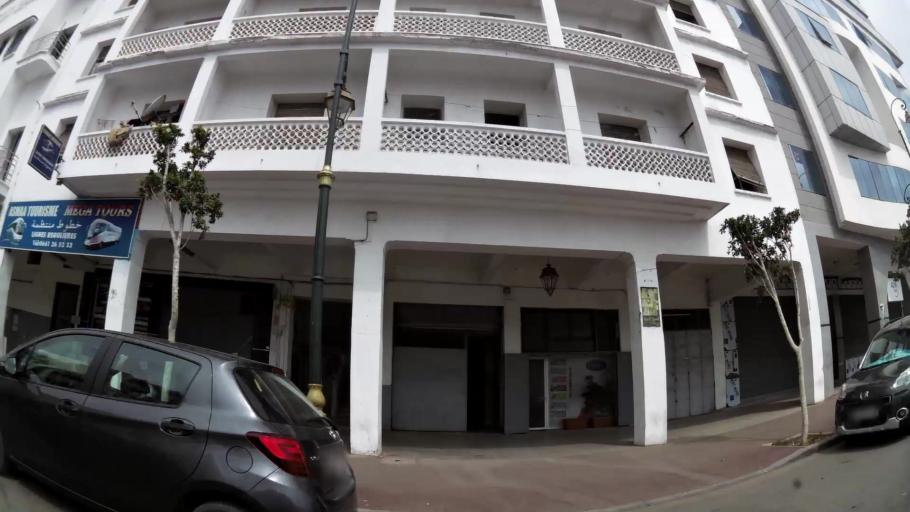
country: MA
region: Rabat-Sale-Zemmour-Zaer
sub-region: Rabat
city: Rabat
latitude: 34.0134
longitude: -6.8485
